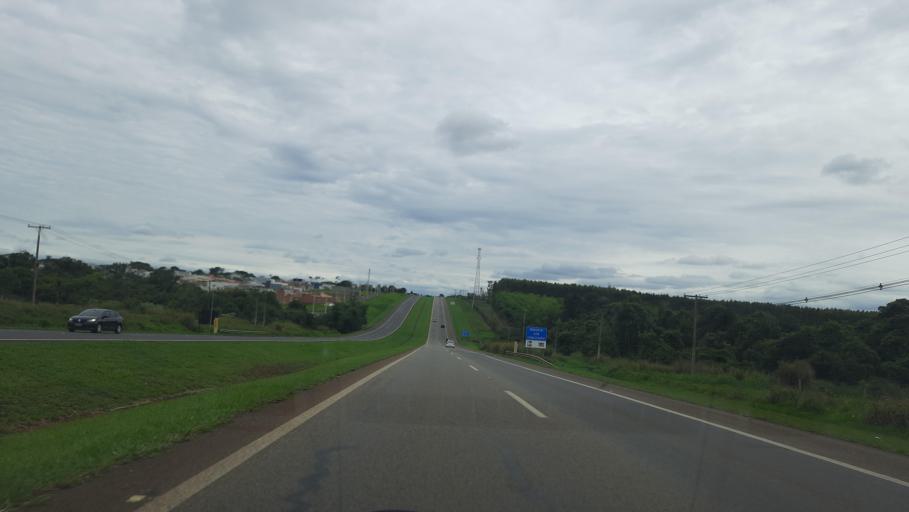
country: BR
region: Sao Paulo
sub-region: Moji-Guacu
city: Mogi-Gaucu
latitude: -22.3328
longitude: -46.9598
